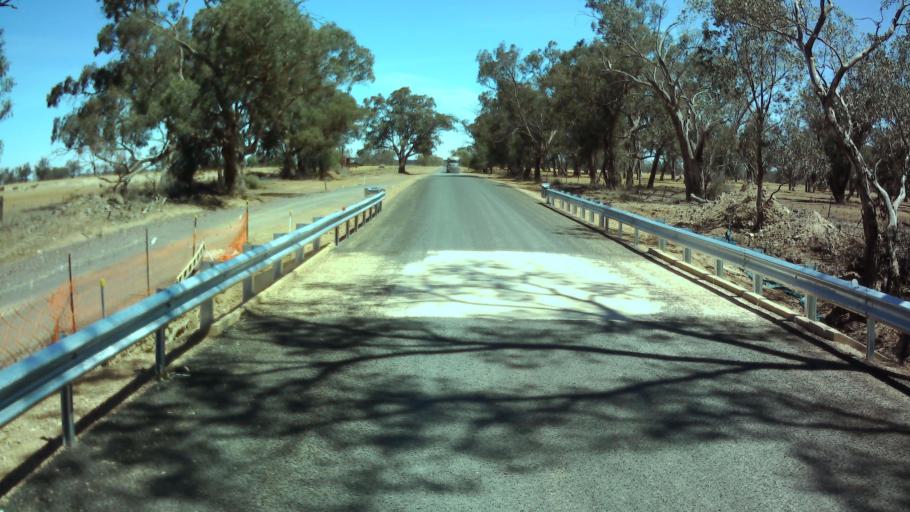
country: AU
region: New South Wales
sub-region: Weddin
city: Grenfell
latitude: -33.8433
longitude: 147.6969
